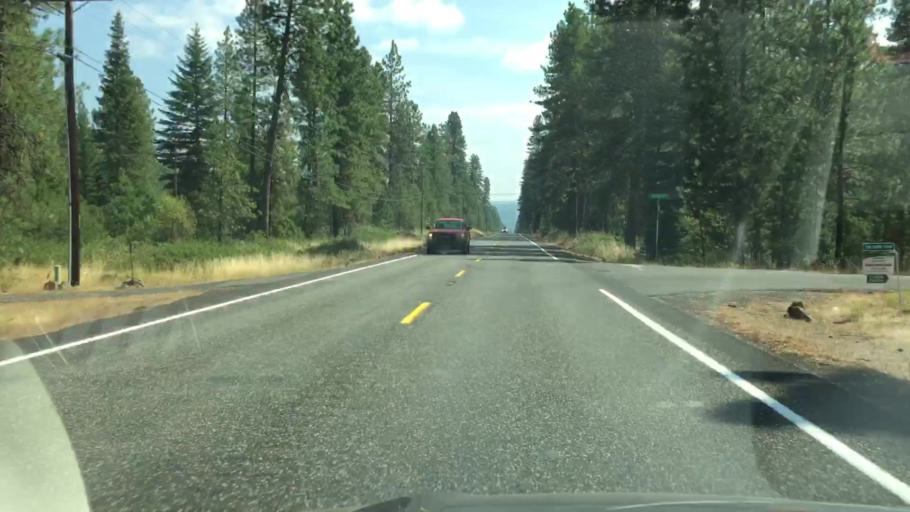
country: US
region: Washington
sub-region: Klickitat County
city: White Salmon
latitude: 45.9831
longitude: -121.5105
